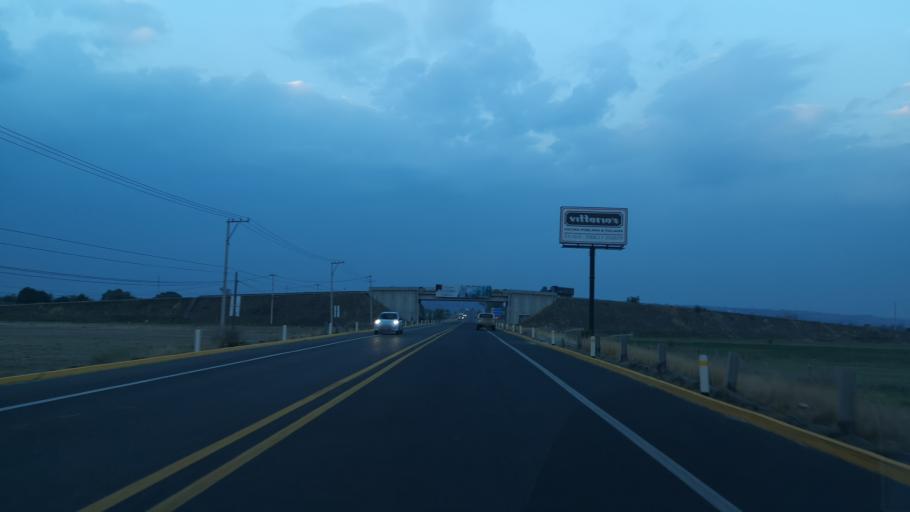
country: MX
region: Puebla
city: Santa Ana Xalmimilulco
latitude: 19.2010
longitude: -98.3634
